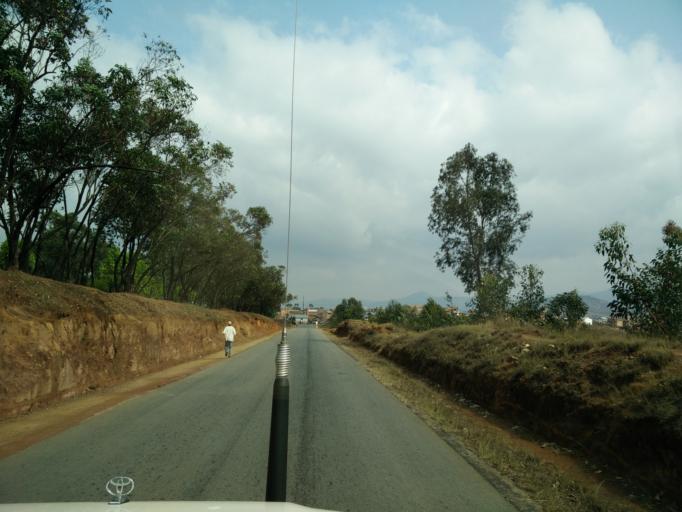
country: MG
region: Upper Matsiatra
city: Fianarantsoa
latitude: -21.3794
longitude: 47.1704
